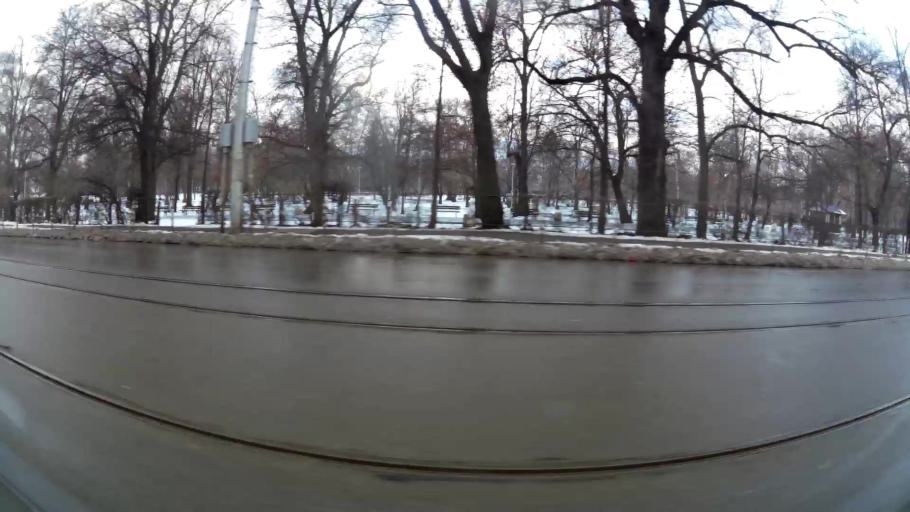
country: BG
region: Sofia-Capital
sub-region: Stolichna Obshtina
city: Sofia
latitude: 42.7056
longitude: 23.2959
